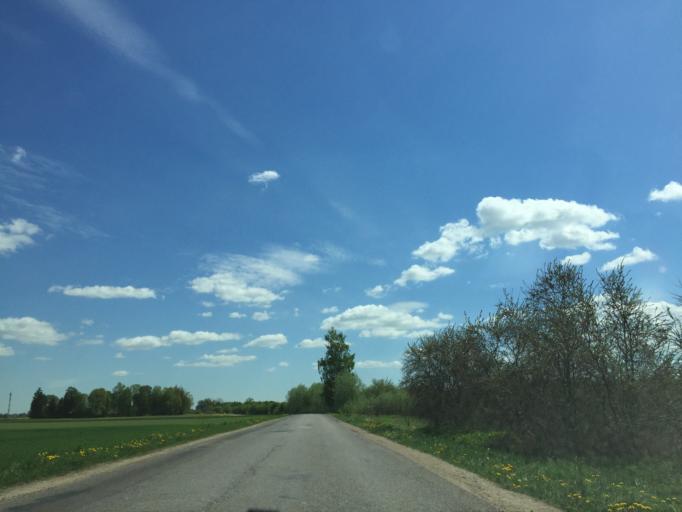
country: LV
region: Bauskas Rajons
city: Bauska
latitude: 56.4116
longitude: 24.1231
